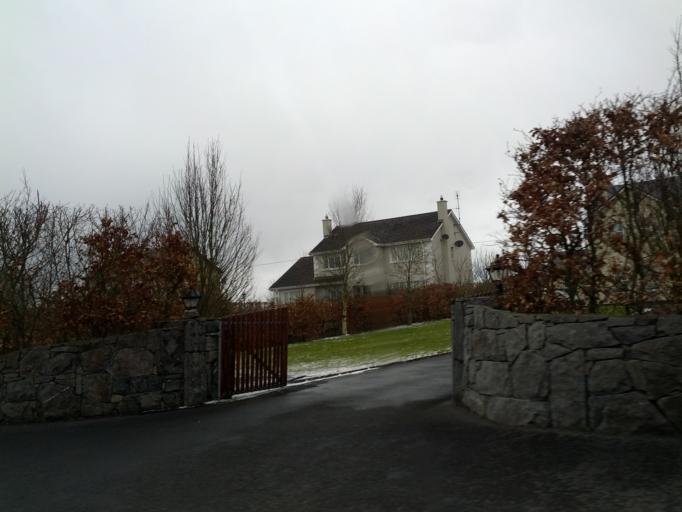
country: IE
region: Connaught
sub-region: County Galway
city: Athenry
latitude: 53.2770
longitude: -8.8042
